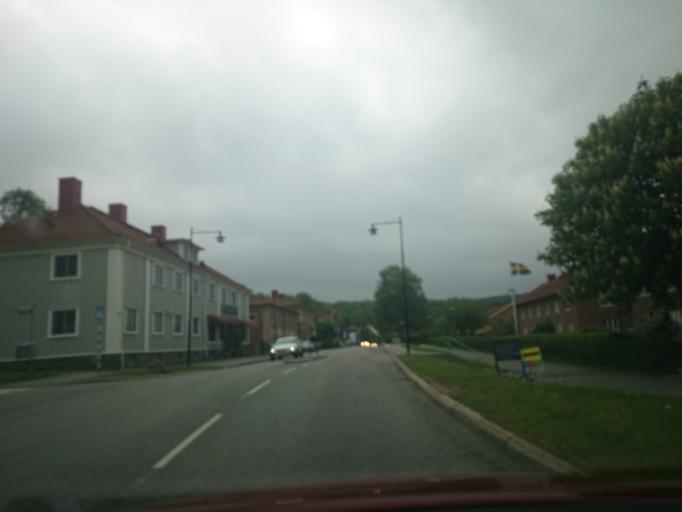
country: SE
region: Vaestra Goetaland
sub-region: Partille Kommun
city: Furulund
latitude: 57.7463
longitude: 12.1755
